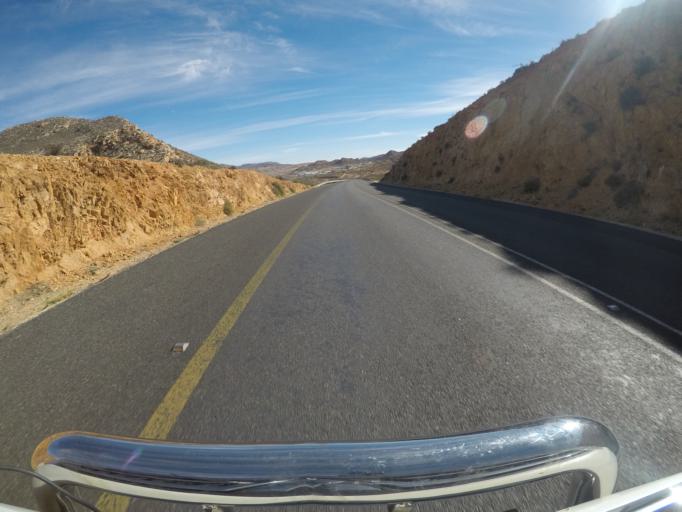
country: ZA
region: Northern Cape
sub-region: Namakwa District Municipality
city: Springbok
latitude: -29.6585
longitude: 17.8910
